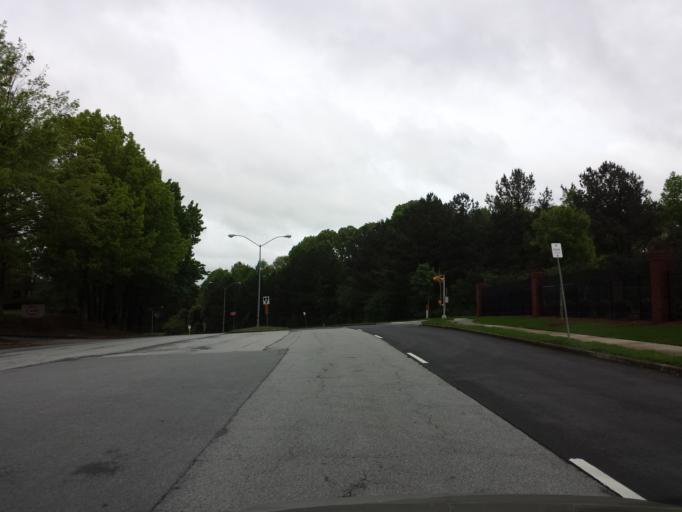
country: US
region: Georgia
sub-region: Cobb County
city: Smyrna
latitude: 33.8326
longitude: -84.5163
